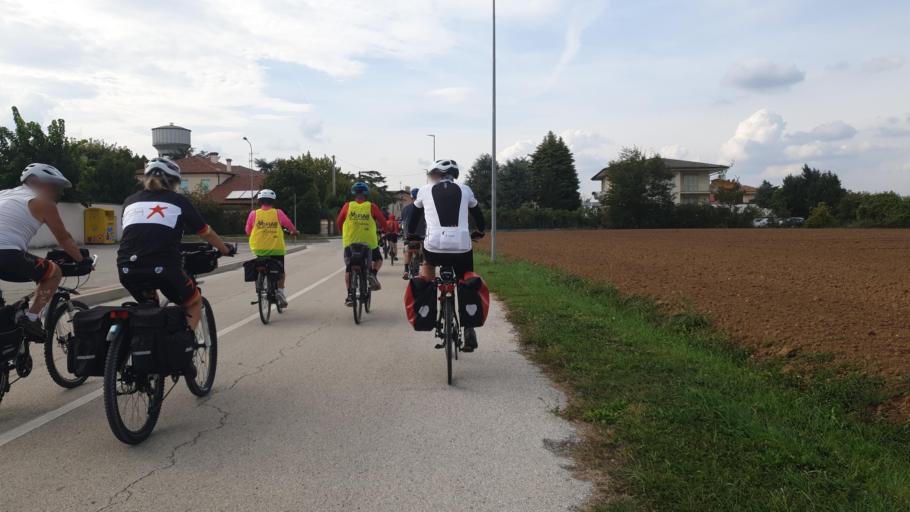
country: IT
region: Veneto
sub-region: Provincia di Vicenza
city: Poiana Maggiore
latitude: 45.2910
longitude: 11.5056
